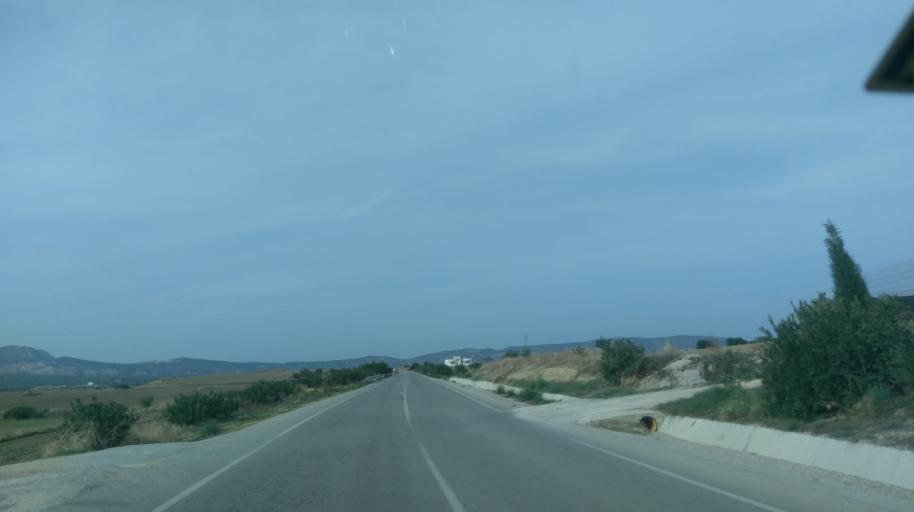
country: CY
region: Ammochostos
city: Leonarisso
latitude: 35.3872
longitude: 34.0107
